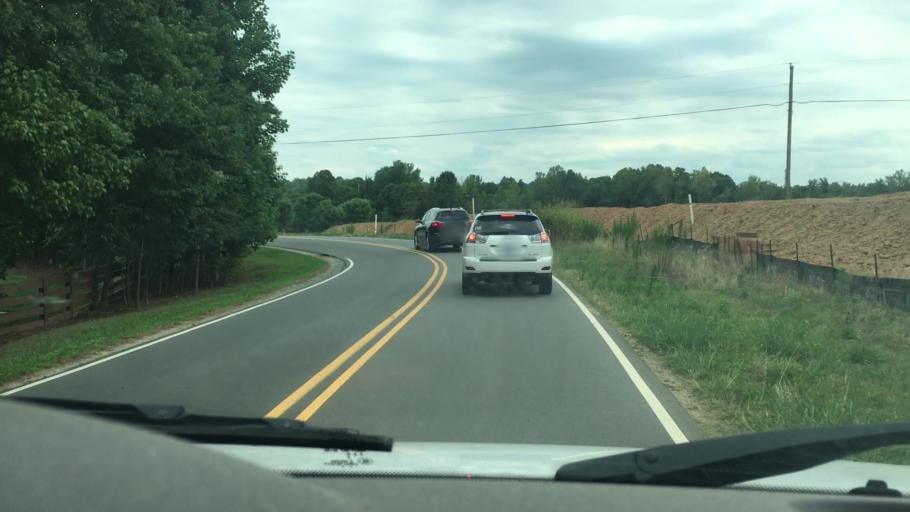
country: US
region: North Carolina
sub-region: Gaston County
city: Davidson
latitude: 35.4600
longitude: -80.7897
